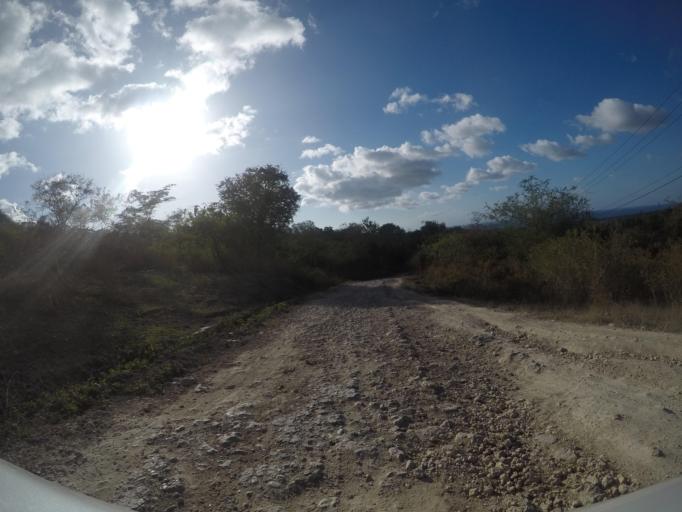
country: TL
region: Lautem
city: Lospalos
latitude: -8.4349
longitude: 126.8493
